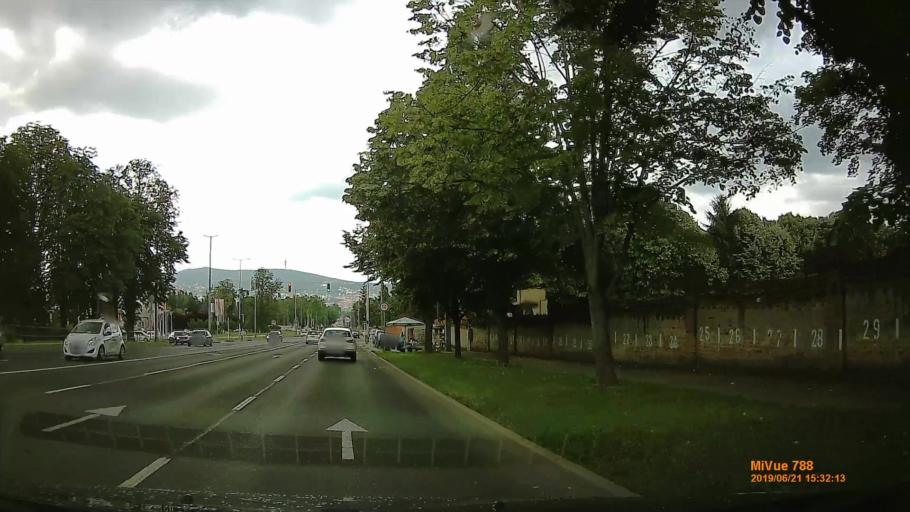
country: HU
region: Baranya
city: Pecs
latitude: 46.0484
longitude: 18.2317
